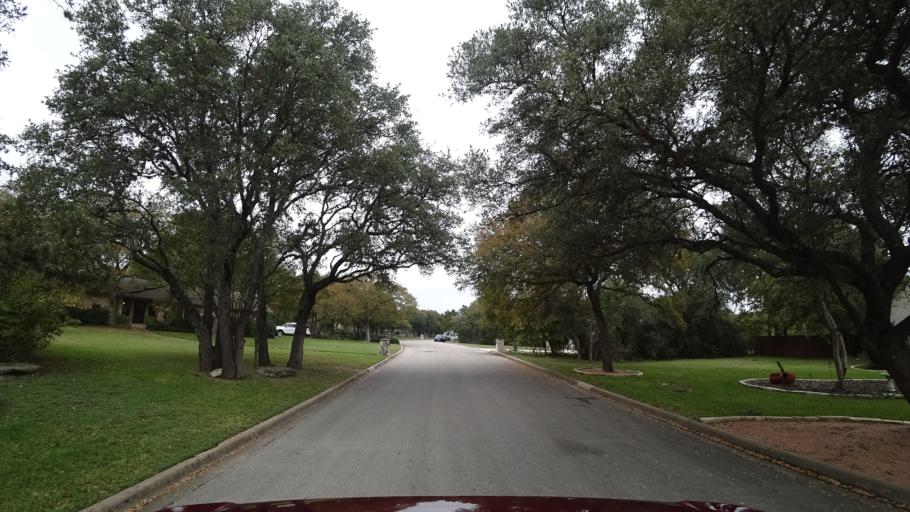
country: US
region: Texas
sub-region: Williamson County
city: Anderson Mill
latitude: 30.4407
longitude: -97.8188
